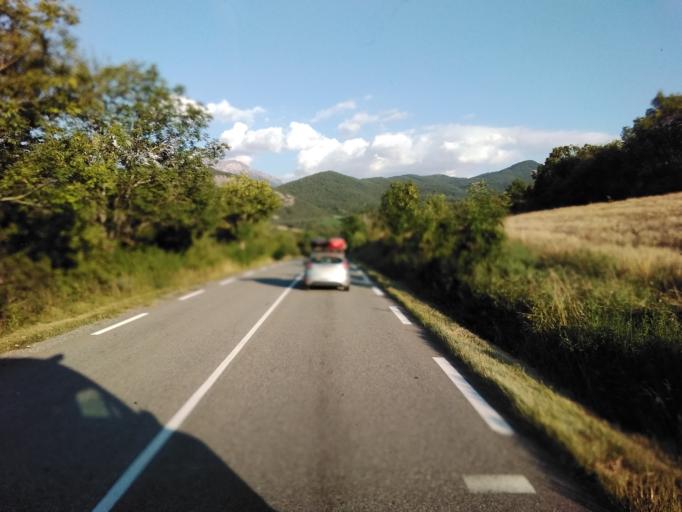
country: FR
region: Provence-Alpes-Cote d'Azur
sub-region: Departement des Hautes-Alpes
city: Chorges
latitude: 44.4547
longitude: 6.2943
